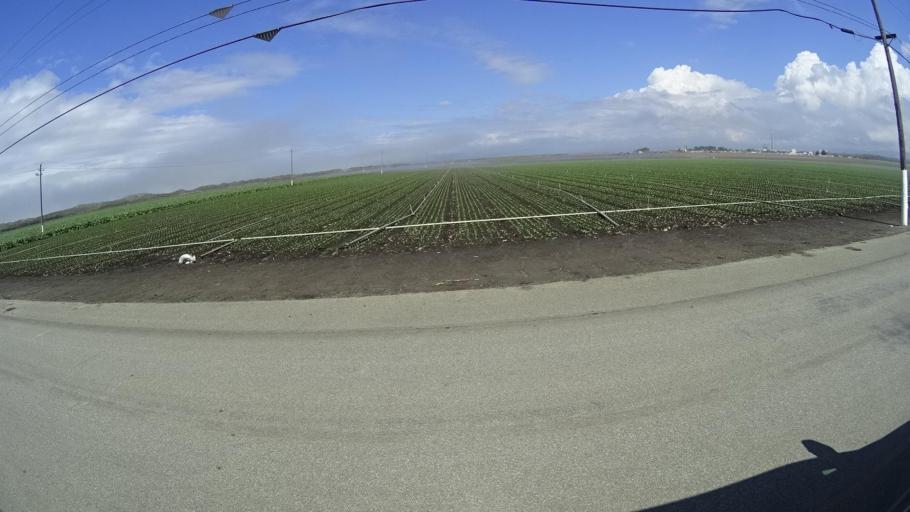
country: US
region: California
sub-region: Monterey County
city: Castroville
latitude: 36.7746
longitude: -121.7853
